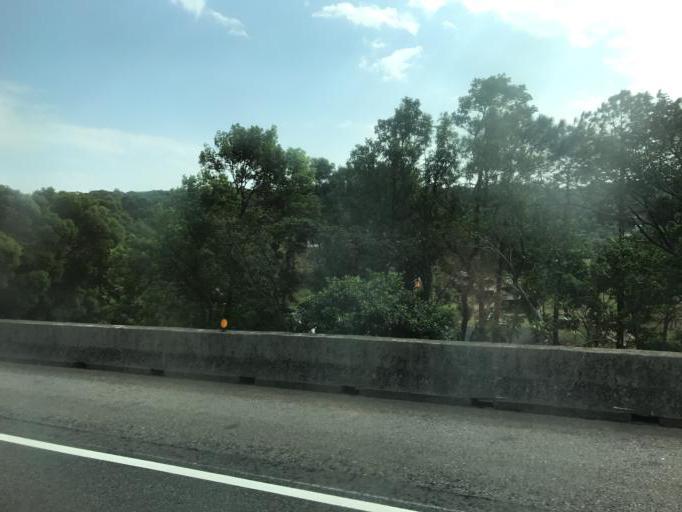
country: TW
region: Taiwan
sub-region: Hsinchu
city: Zhubei
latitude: 24.8768
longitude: 121.0445
